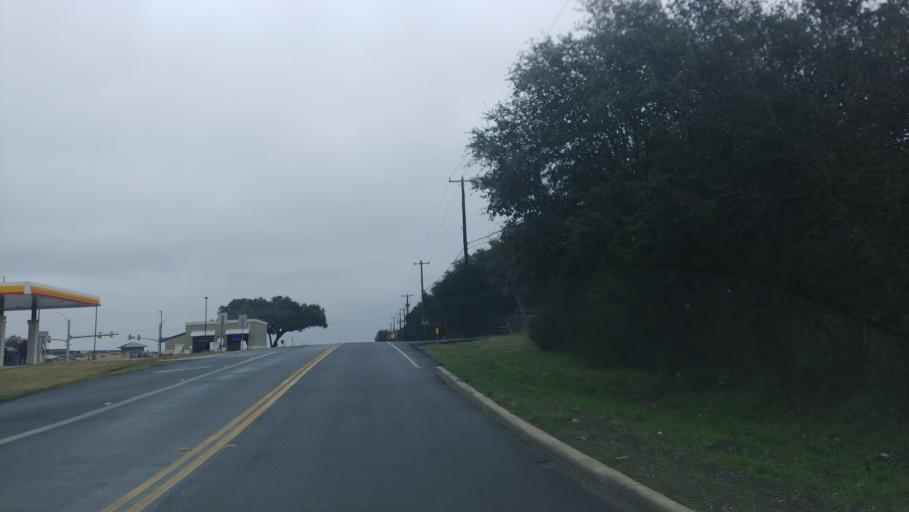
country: US
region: Texas
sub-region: Bexar County
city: Helotes
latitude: 29.5645
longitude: -98.6894
